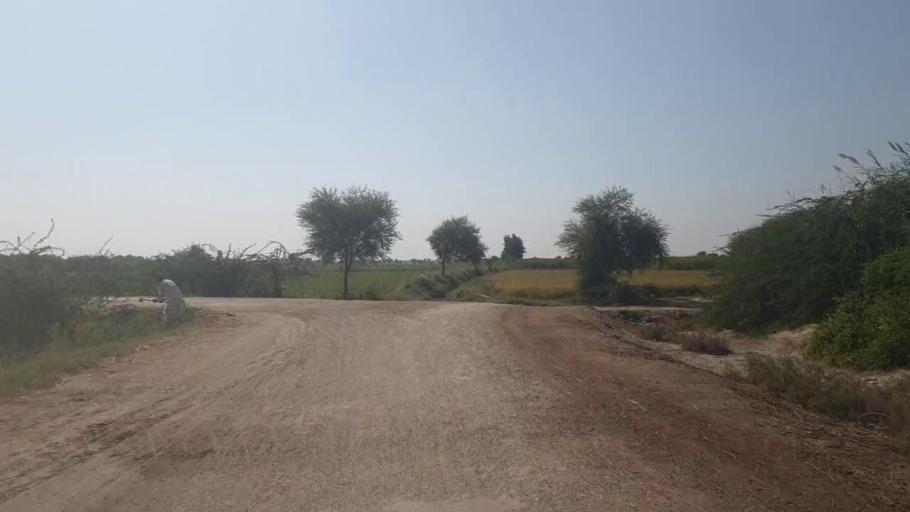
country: PK
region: Sindh
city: Badin
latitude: 24.5760
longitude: 68.8433
